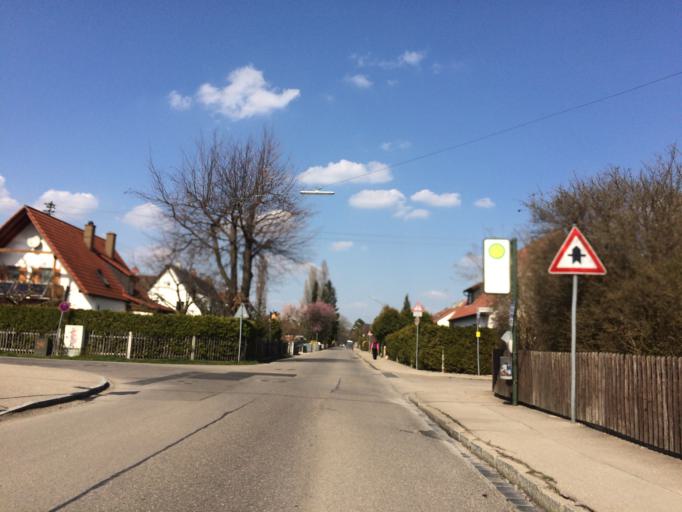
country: DE
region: Bavaria
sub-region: Swabia
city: Gersthofen
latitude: 48.4058
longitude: 10.8963
